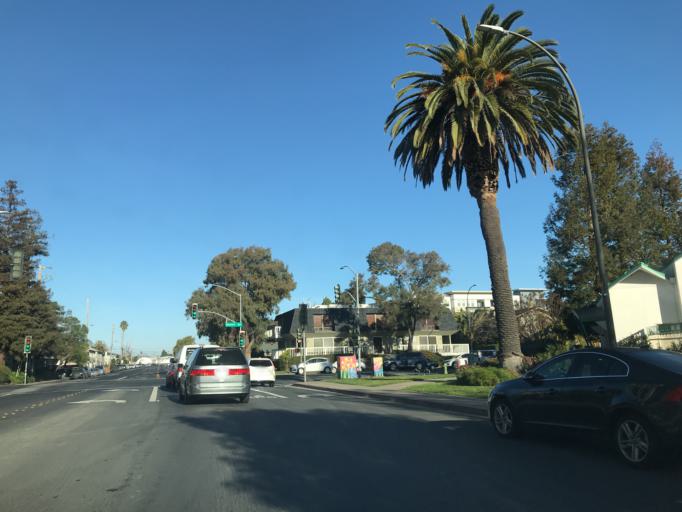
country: US
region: California
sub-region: San Mateo County
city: Redwood City
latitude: 37.4900
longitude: -122.2314
